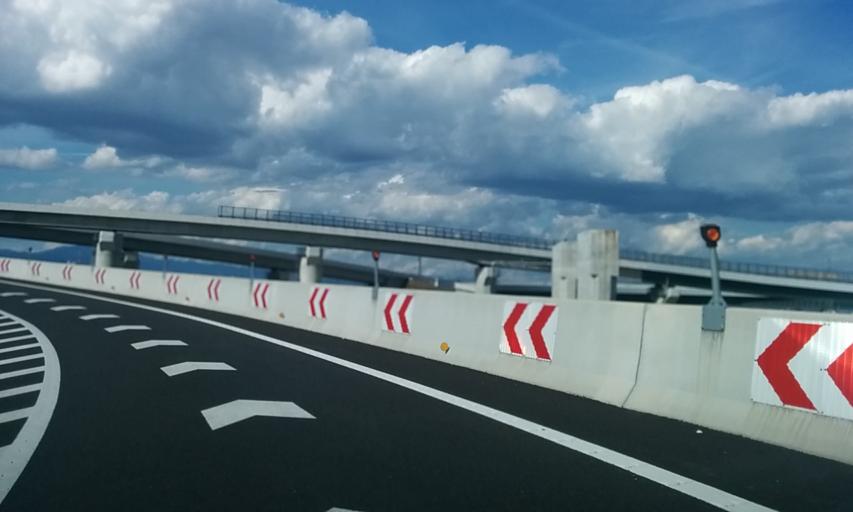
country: JP
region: Kyoto
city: Tanabe
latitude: 34.8457
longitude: 135.7609
